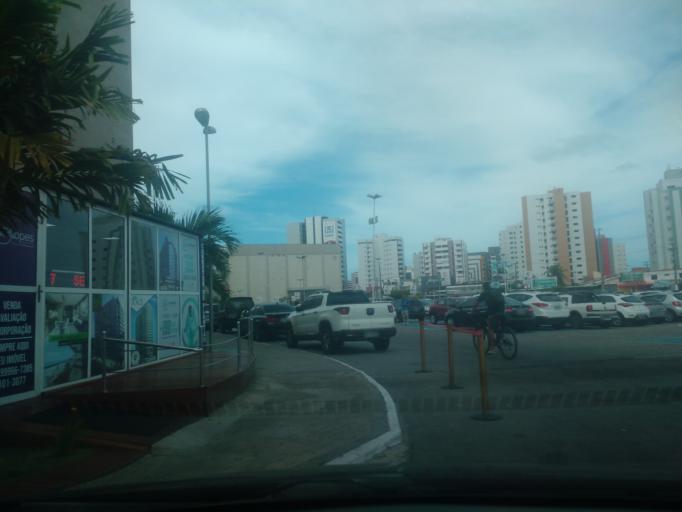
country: BR
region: Alagoas
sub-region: Maceio
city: Maceio
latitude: -9.6488
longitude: -35.7154
